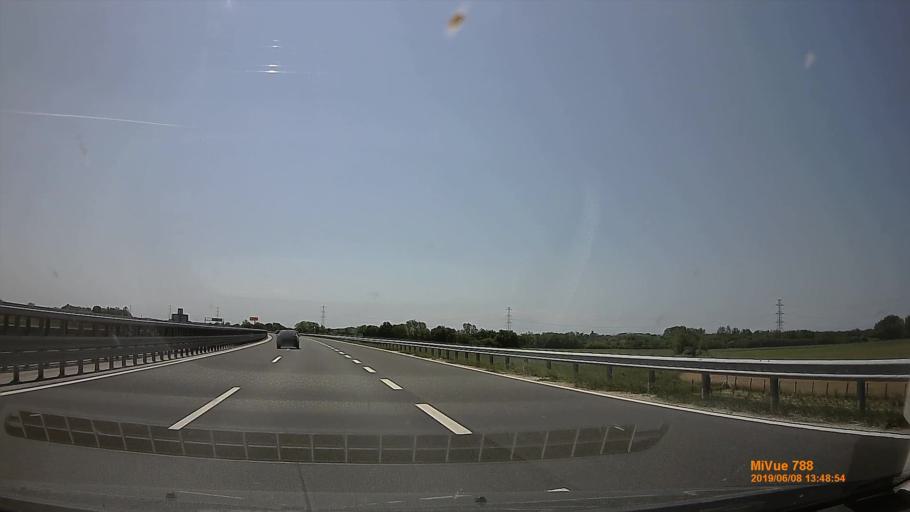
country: HU
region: Vas
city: Repcelak
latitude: 47.4083
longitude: 17.0114
